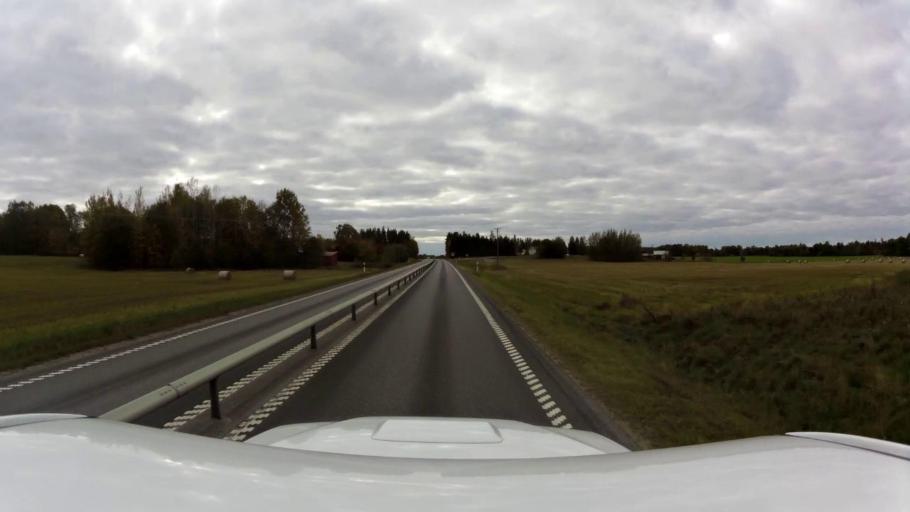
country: SE
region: OEstergoetland
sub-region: Linkopings Kommun
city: Malmslatt
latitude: 58.3603
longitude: 15.5453
